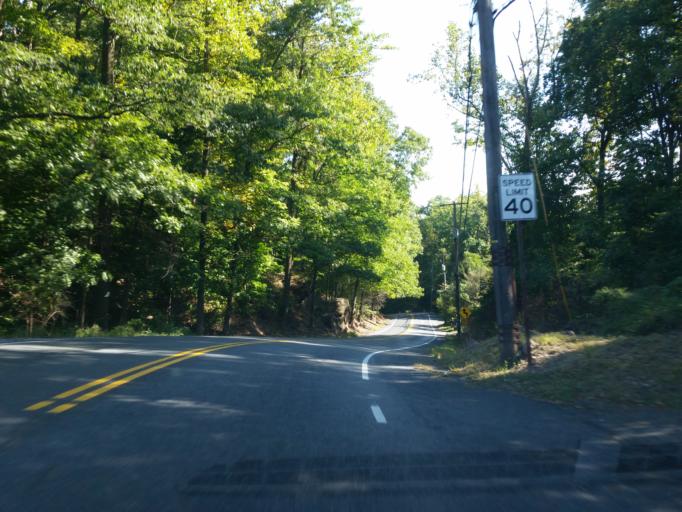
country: US
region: Pennsylvania
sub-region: Berks County
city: Alleghenyville
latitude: 40.2424
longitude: -75.9955
